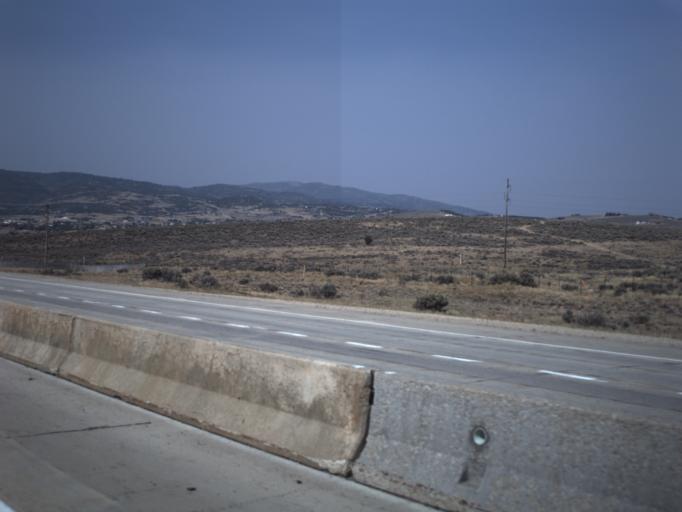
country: US
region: Utah
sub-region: Summit County
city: Snyderville
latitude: 40.7250
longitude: -111.4924
